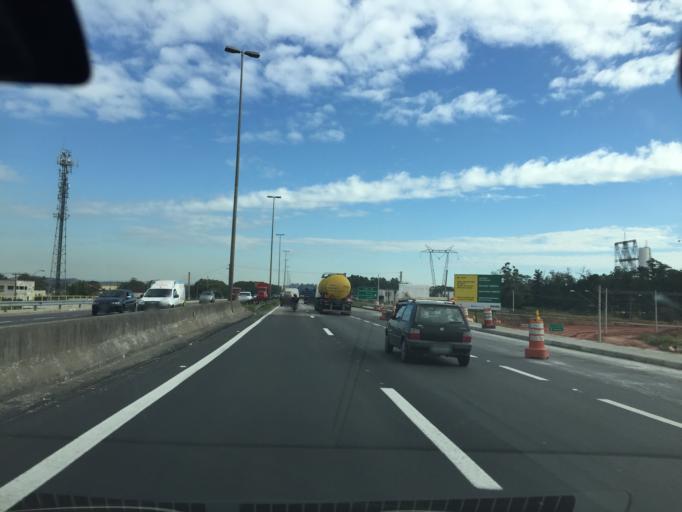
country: BR
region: Sao Paulo
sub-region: Jacarei
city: Jacarei
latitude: -23.2784
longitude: -45.9796
